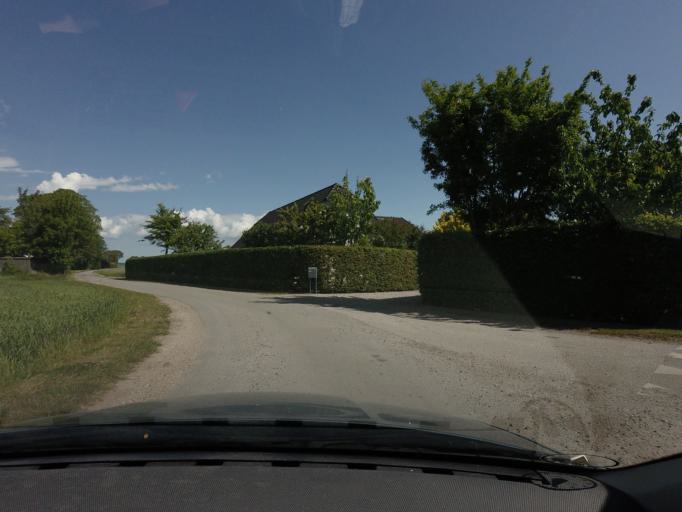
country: DK
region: Central Jutland
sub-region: Norddjurs Kommune
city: Grenaa
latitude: 56.4812
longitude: 10.8725
